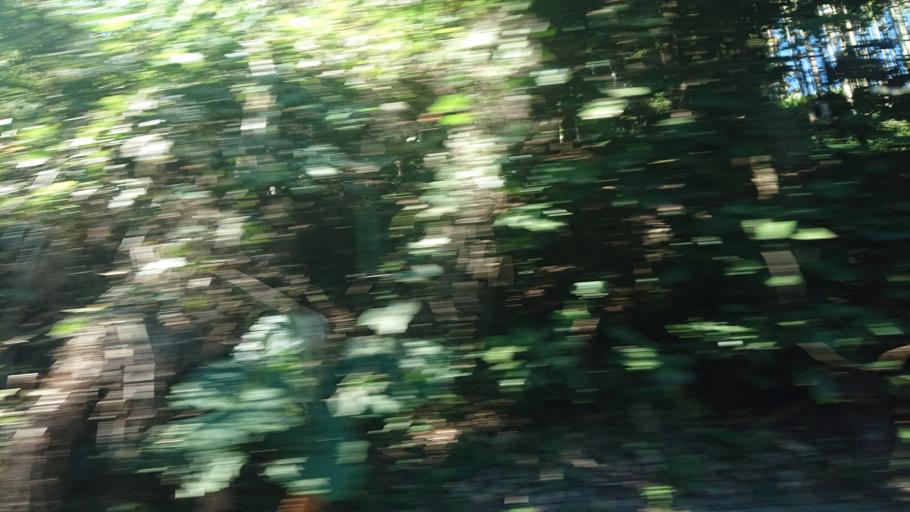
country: TW
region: Taiwan
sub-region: Chiayi
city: Jiayi Shi
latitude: 23.5322
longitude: 120.6448
